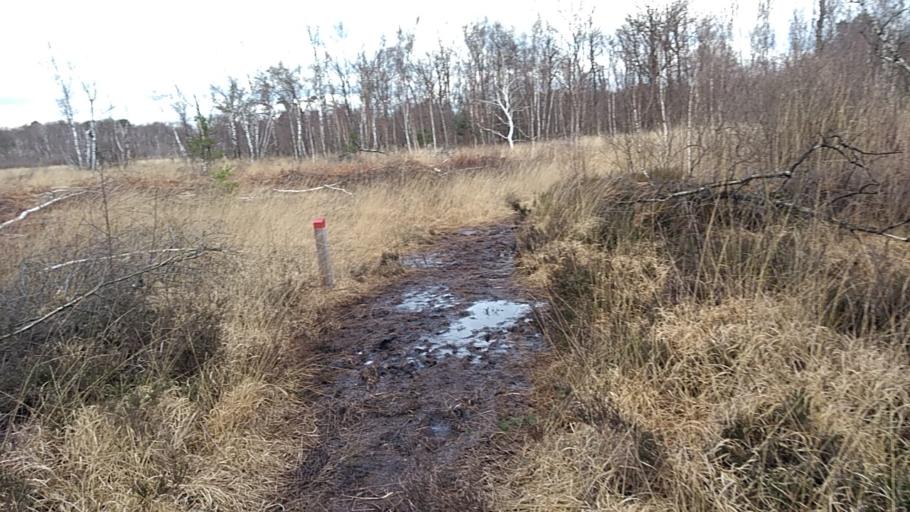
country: NL
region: Gelderland
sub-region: Gemeente Winterswijk
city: Winterswijk
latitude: 51.9931
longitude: 6.6606
